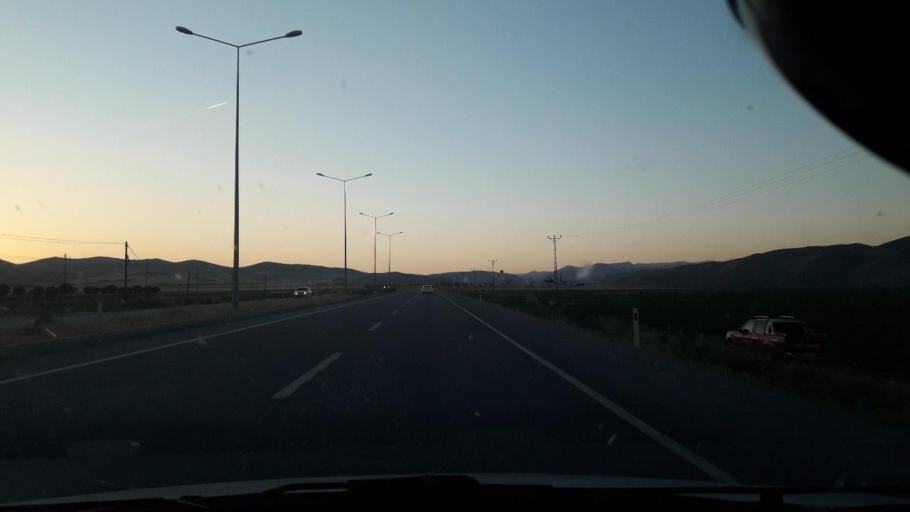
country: TR
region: Malatya
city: Yazihan
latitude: 38.6045
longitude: 38.1790
